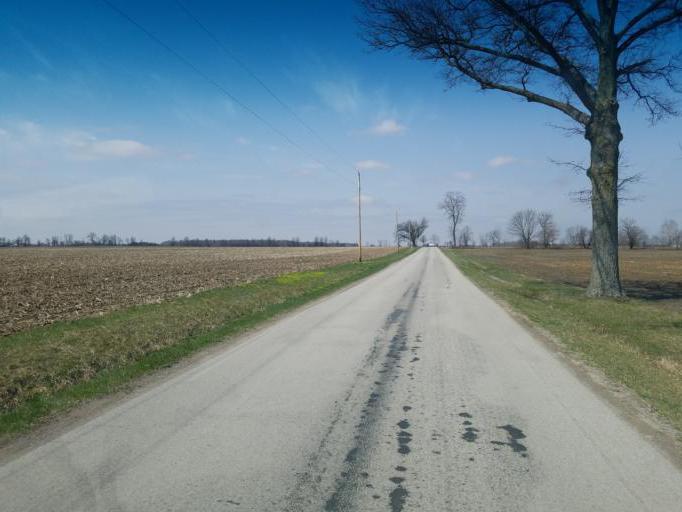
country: US
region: Ohio
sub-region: Wyandot County
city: Carey
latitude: 40.8611
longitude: -83.4046
